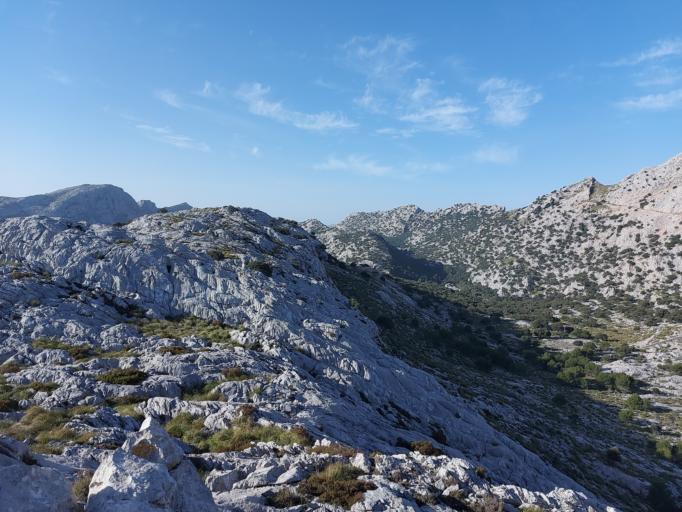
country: ES
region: Balearic Islands
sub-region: Illes Balears
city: Fornalutx
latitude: 39.7971
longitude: 2.7999
